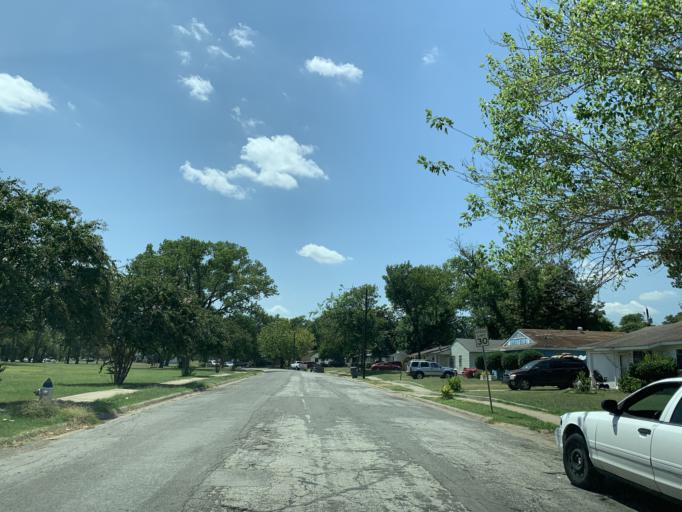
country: US
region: Texas
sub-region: Dallas County
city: Hutchins
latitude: 32.6842
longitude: -96.7783
